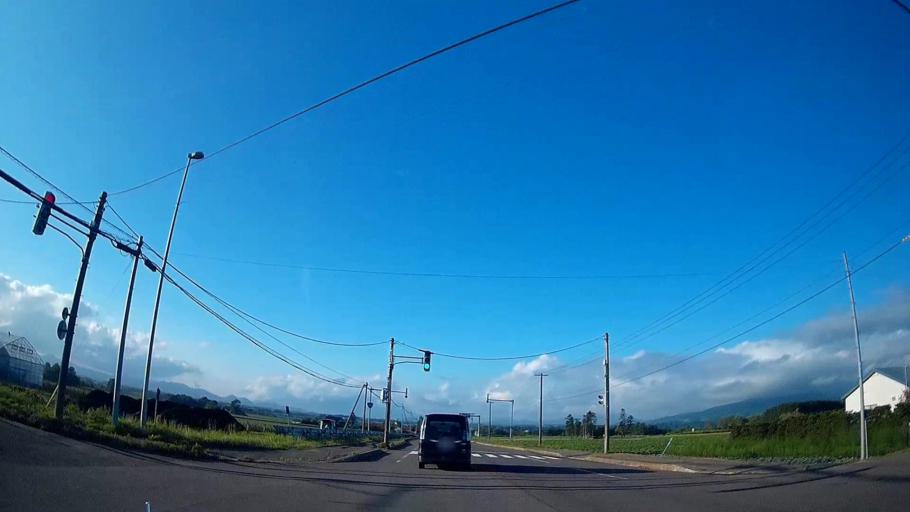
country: JP
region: Hokkaido
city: Date
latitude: 42.6337
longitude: 140.8010
